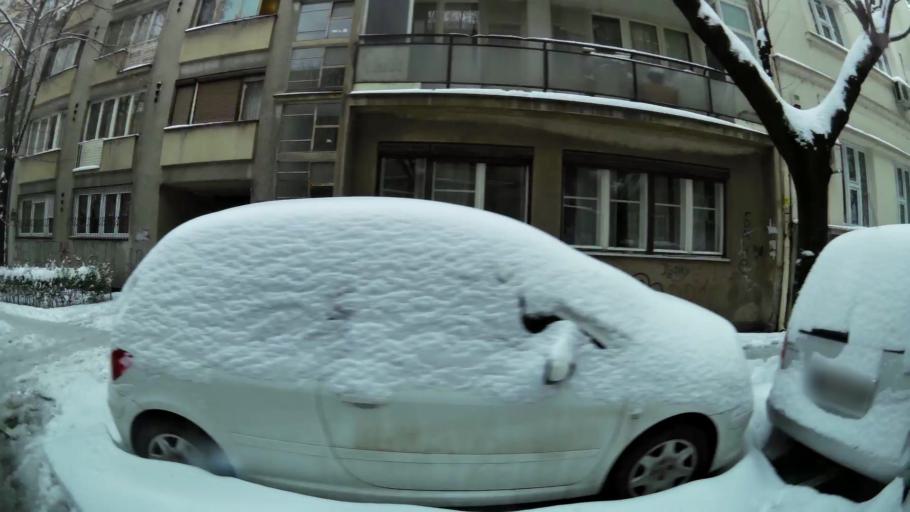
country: RS
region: Central Serbia
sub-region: Belgrade
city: Stari Grad
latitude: 44.8185
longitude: 20.4694
